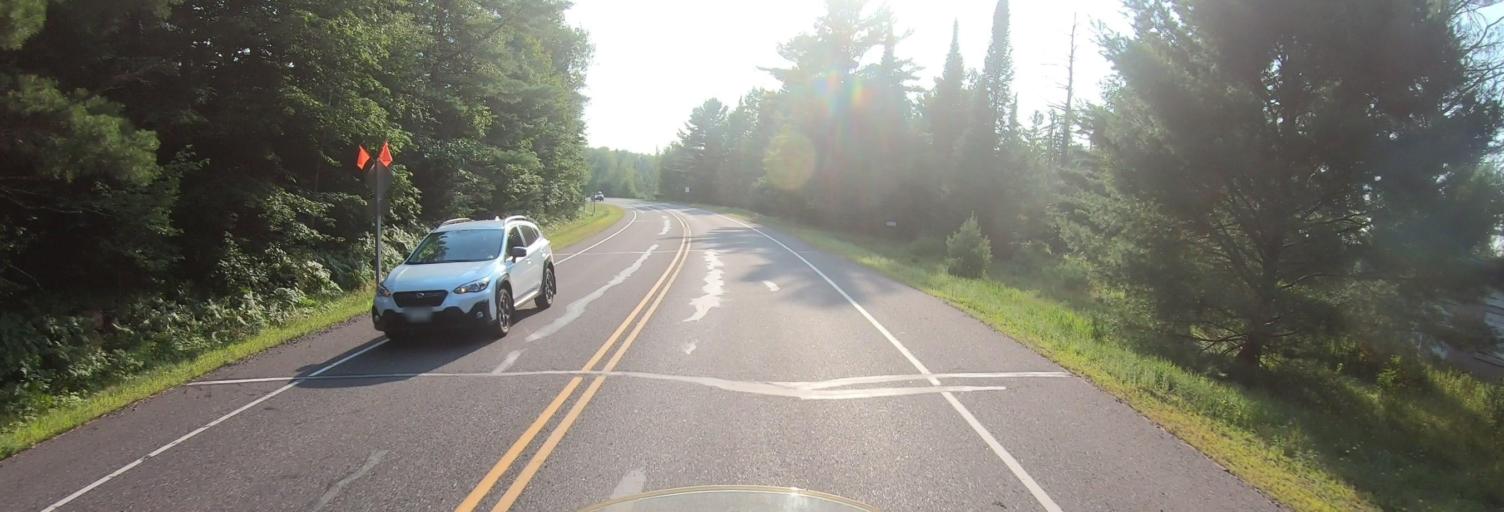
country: US
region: Wisconsin
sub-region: Ashland County
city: Ashland
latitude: 46.1665
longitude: -90.9126
